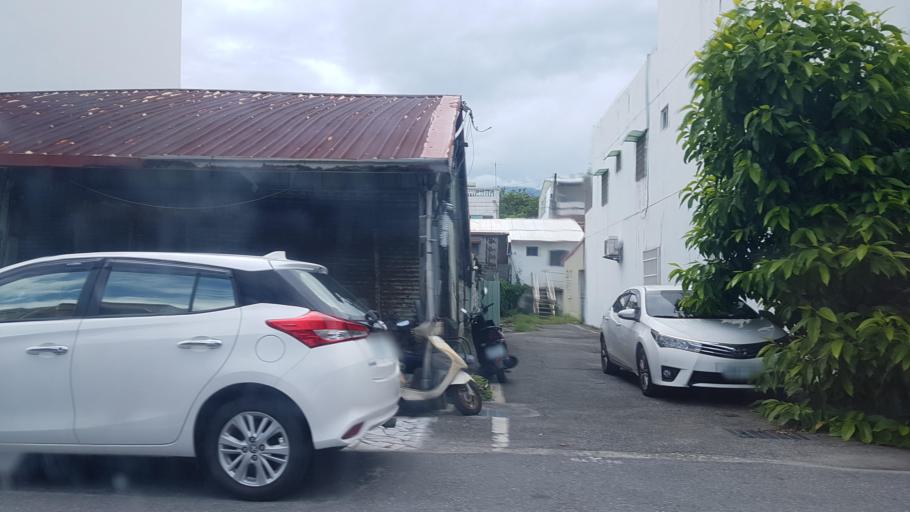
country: TW
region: Taiwan
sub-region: Hualien
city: Hualian
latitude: 23.9759
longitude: 121.6156
